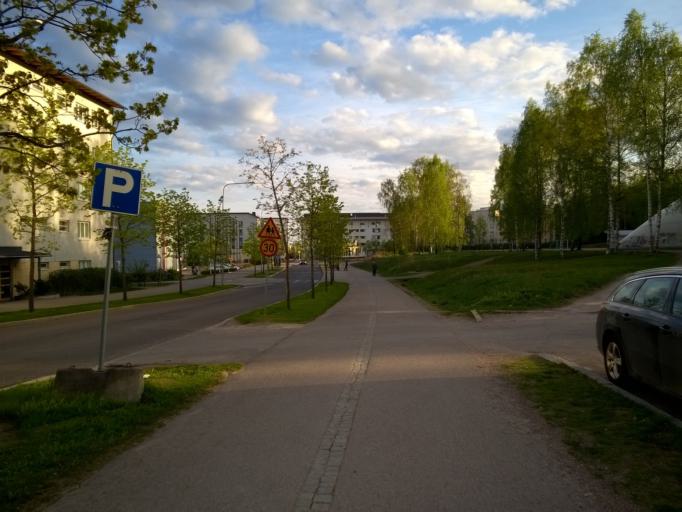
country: FI
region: Uusimaa
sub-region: Helsinki
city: Vantaa
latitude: 60.2290
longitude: 25.0283
